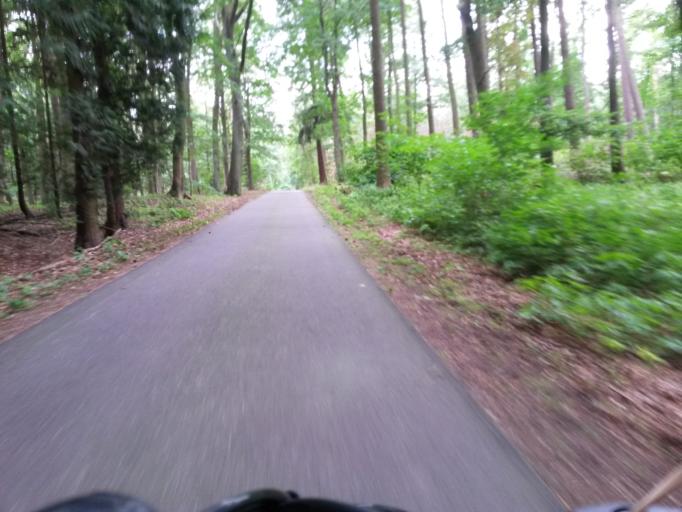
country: DE
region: Brandenburg
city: Angermunde
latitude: 53.0513
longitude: 13.9422
